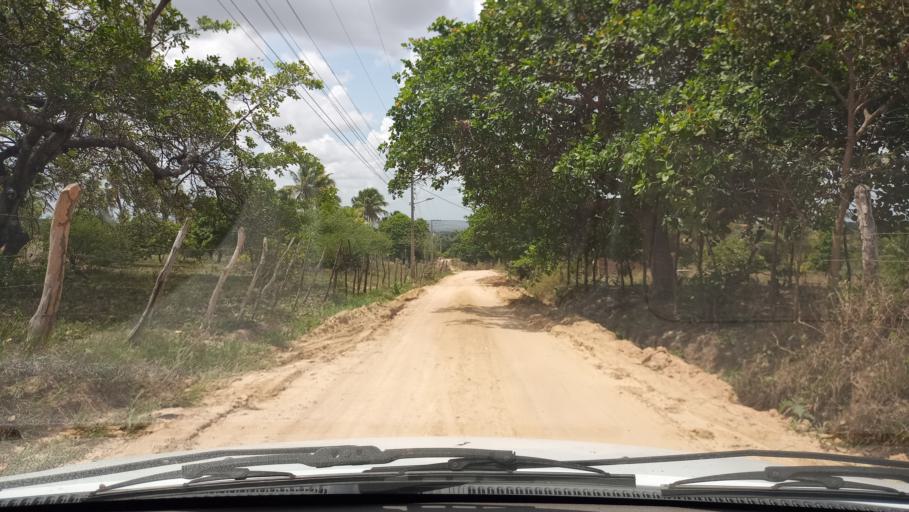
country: BR
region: Rio Grande do Norte
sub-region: Brejinho
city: Brejinho
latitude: -6.2521
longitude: -35.3367
